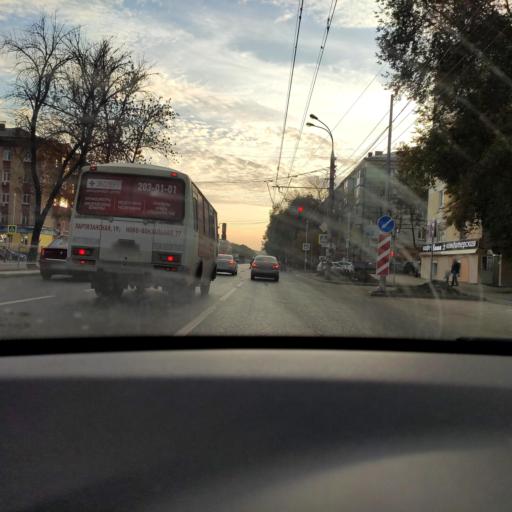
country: RU
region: Samara
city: Samara
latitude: 53.2090
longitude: 50.2399
